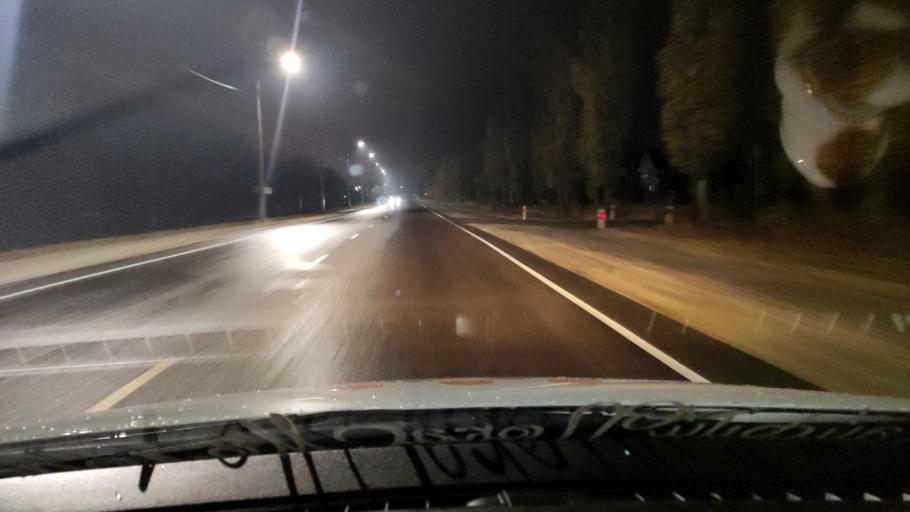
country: RU
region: Voronezj
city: Semiluki
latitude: 51.7126
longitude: 39.0271
